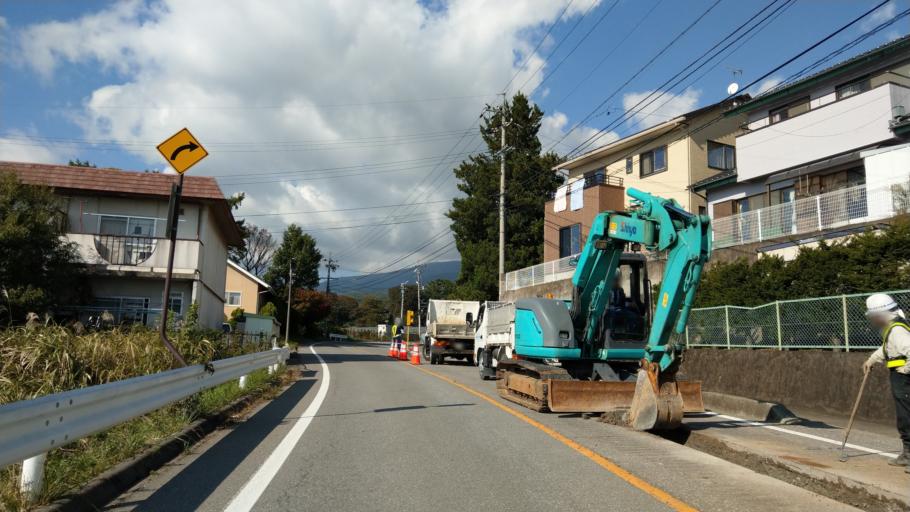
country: JP
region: Nagano
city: Komoro
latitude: 36.3380
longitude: 138.4277
